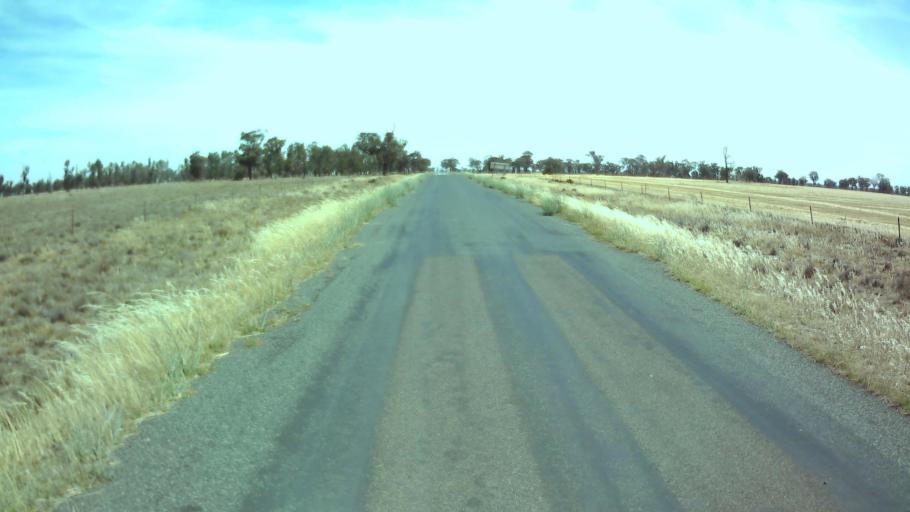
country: AU
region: New South Wales
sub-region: Weddin
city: Grenfell
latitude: -33.9972
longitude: 147.7748
